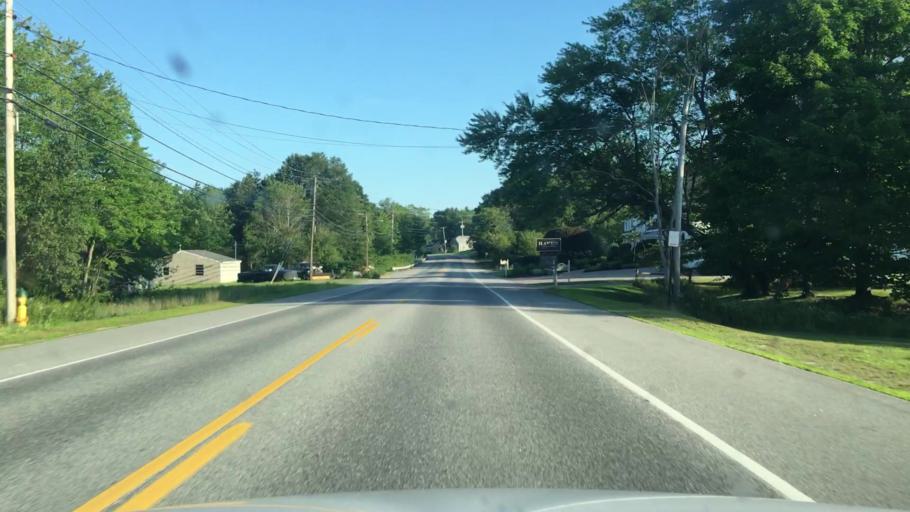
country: US
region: Maine
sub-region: Androscoggin County
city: Lisbon
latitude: 44.0415
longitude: -70.1118
